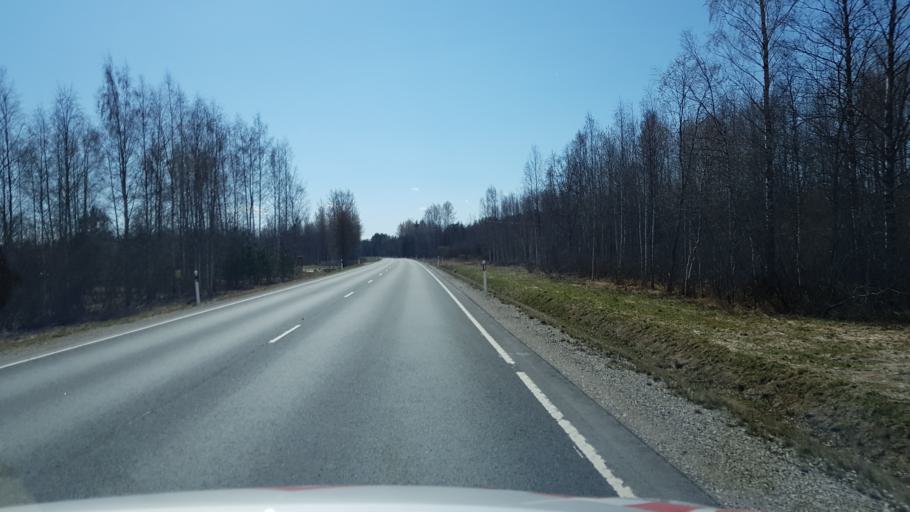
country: EE
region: Jogevamaa
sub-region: Mustvee linn
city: Mustvee
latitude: 58.8832
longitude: 26.9562
